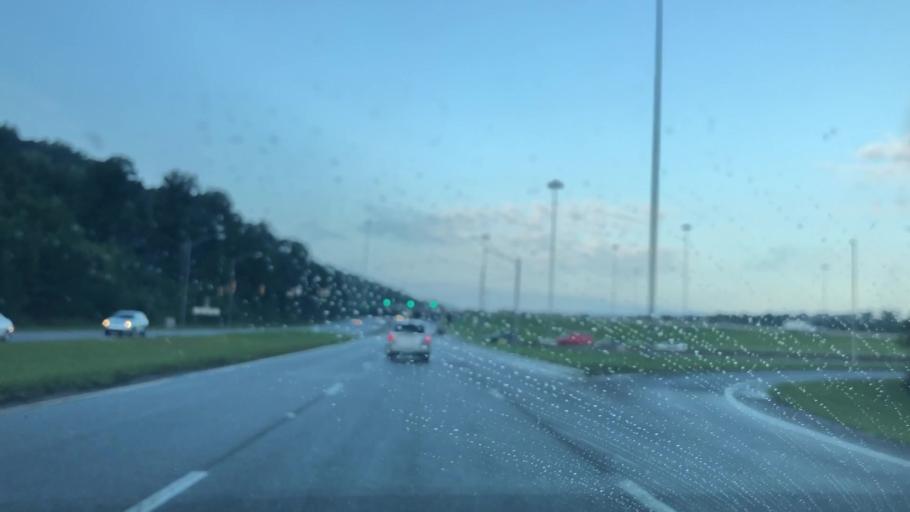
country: US
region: Alabama
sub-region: Shelby County
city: Indian Springs Village
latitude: 33.3573
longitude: -86.7753
